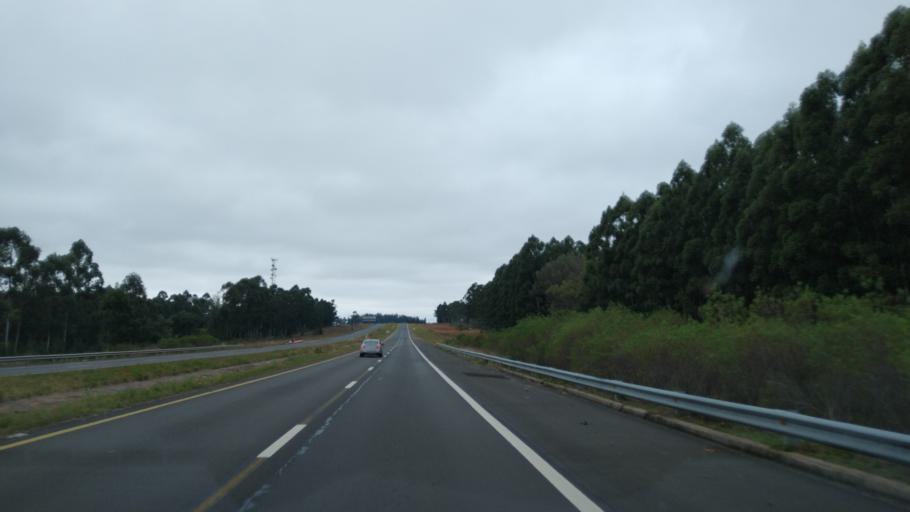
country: AR
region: Corrientes
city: Libertad
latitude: -30.0574
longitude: -57.8087
